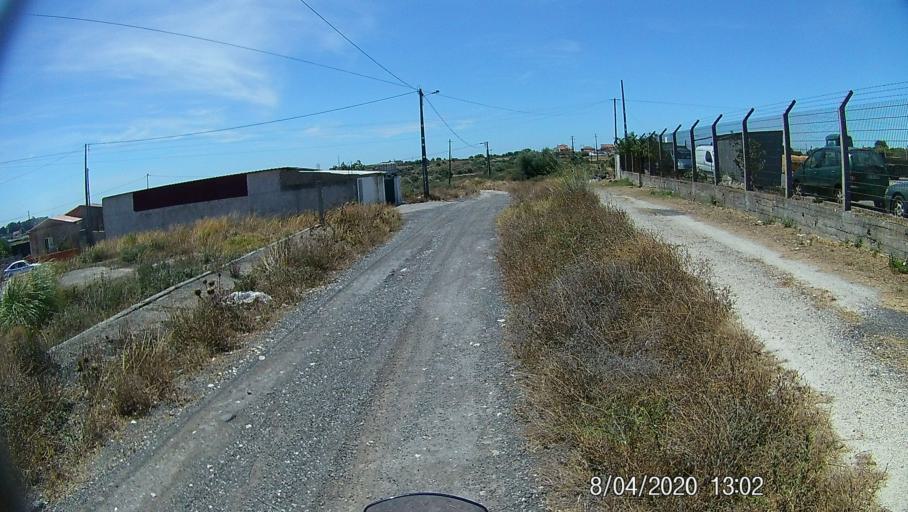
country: PT
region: Lisbon
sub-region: Sintra
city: Rio de Mouro
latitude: 38.7429
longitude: -9.3535
